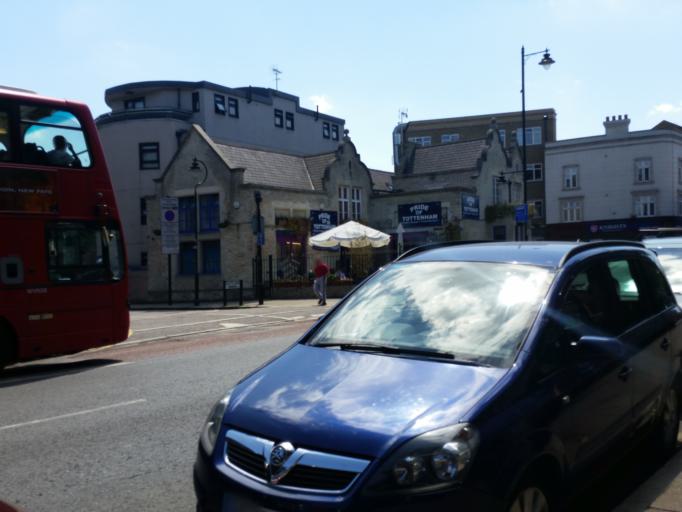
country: GB
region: England
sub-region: Greater London
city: Harringay
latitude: 51.5973
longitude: -0.0682
